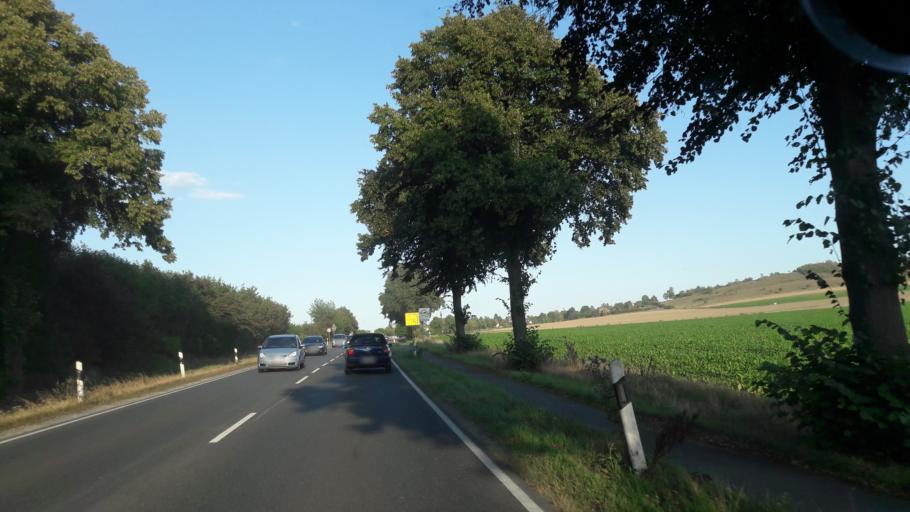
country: DE
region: Lower Saxony
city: Giesen
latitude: 52.1595
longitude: 9.8926
